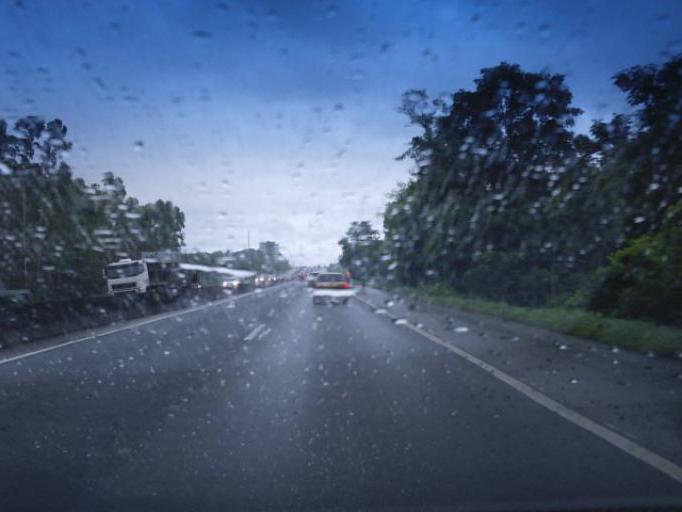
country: BR
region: Santa Catarina
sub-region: Barra Velha
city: Barra Velha
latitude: -26.6943
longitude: -48.6981
